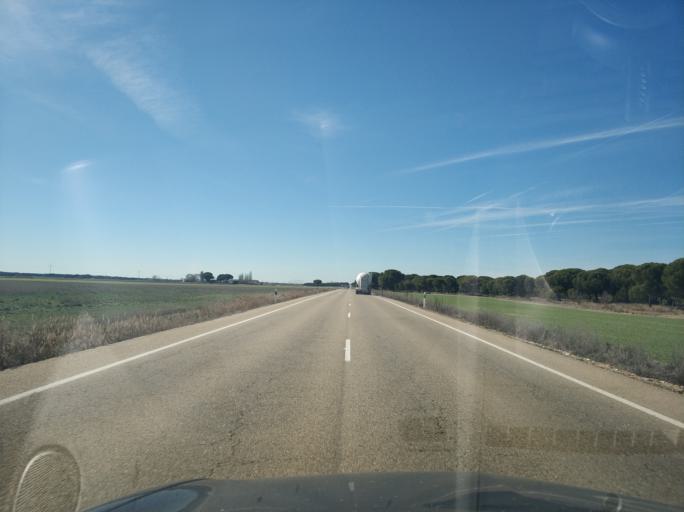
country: ES
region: Castille and Leon
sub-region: Provincia de Valladolid
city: Aldeamayor de San Martin
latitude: 41.5567
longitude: -4.6328
